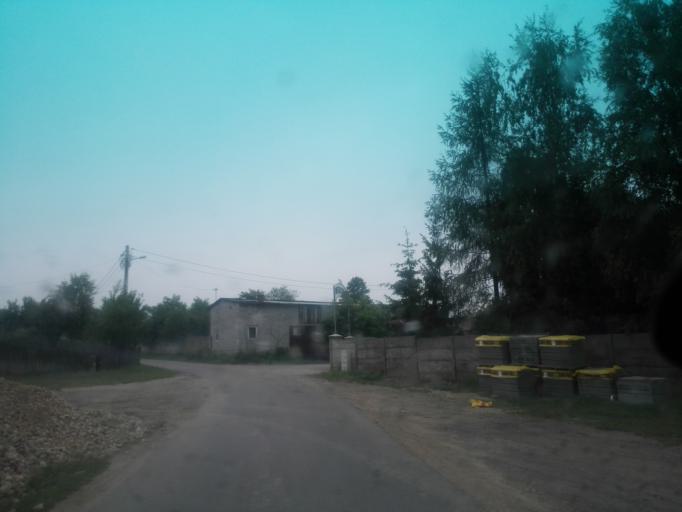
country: PL
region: Silesian Voivodeship
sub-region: Powiat czestochowski
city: Mstow
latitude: 50.8232
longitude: 19.2971
